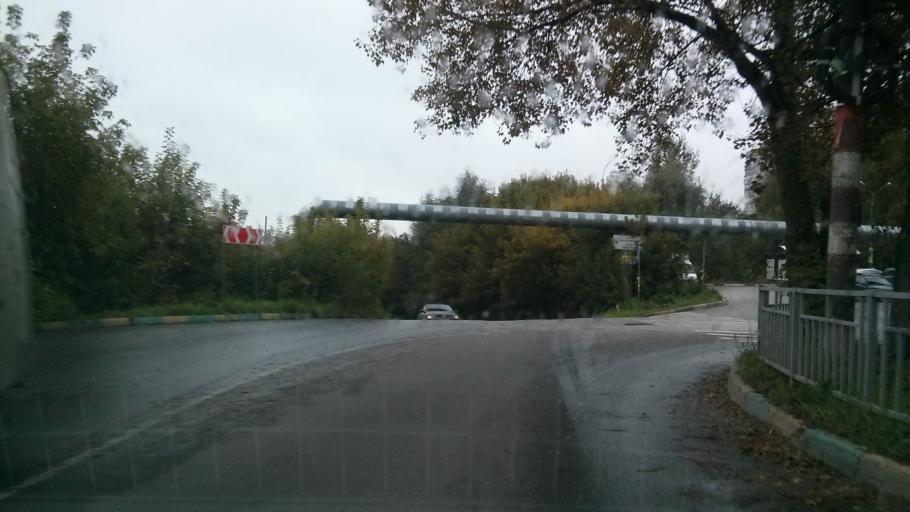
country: RU
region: Nizjnij Novgorod
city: Bor
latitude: 56.3159
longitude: 44.0549
